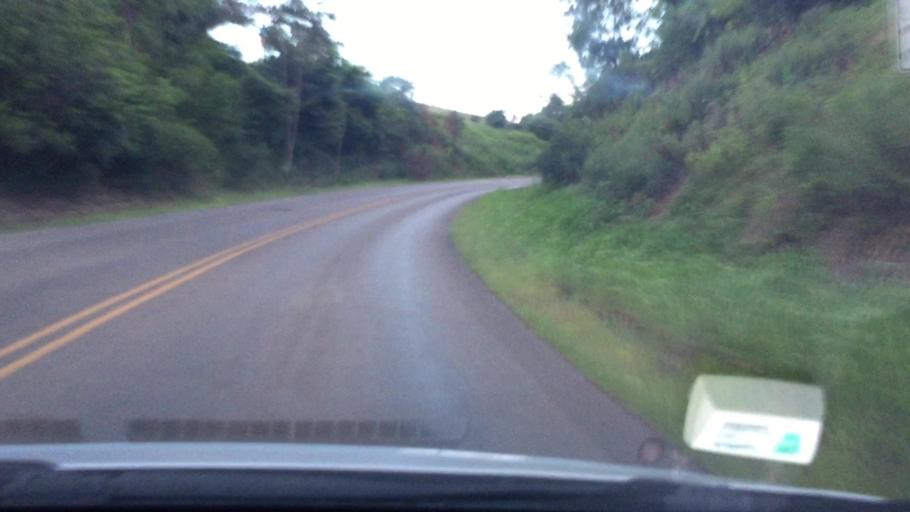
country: US
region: Pennsylvania
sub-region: Allegheny County
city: Monroeville
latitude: 40.4430
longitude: -79.7981
